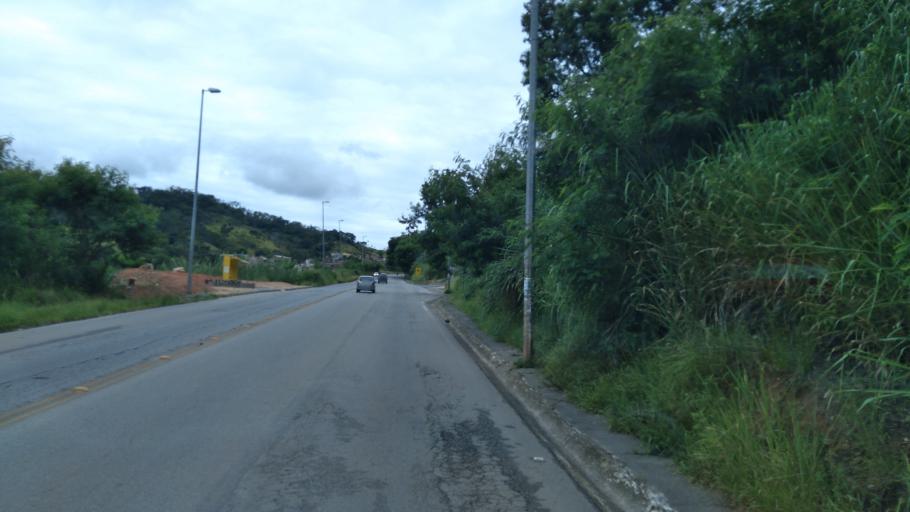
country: BR
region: Minas Gerais
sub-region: Belo Horizonte
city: Belo Horizonte
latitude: -19.8711
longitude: -43.8937
